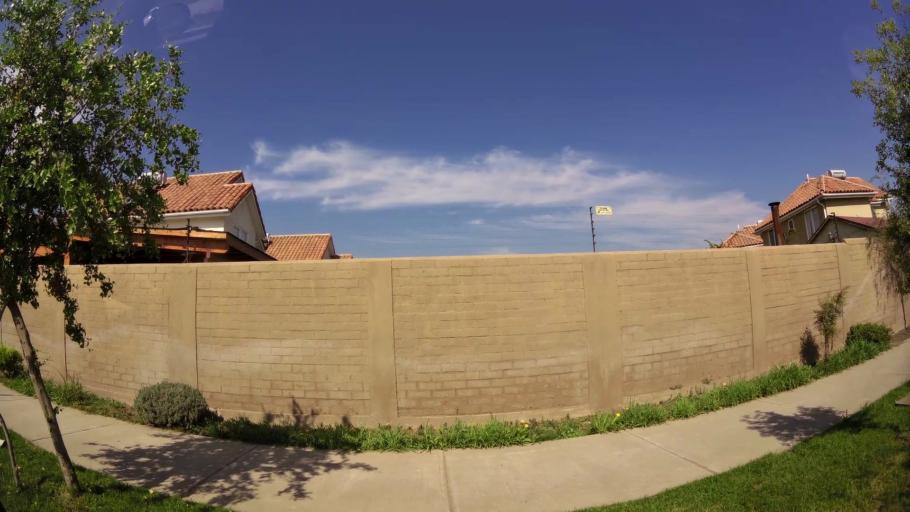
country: CL
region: Santiago Metropolitan
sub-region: Provincia de Talagante
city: Penaflor
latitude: -33.5703
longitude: -70.8286
